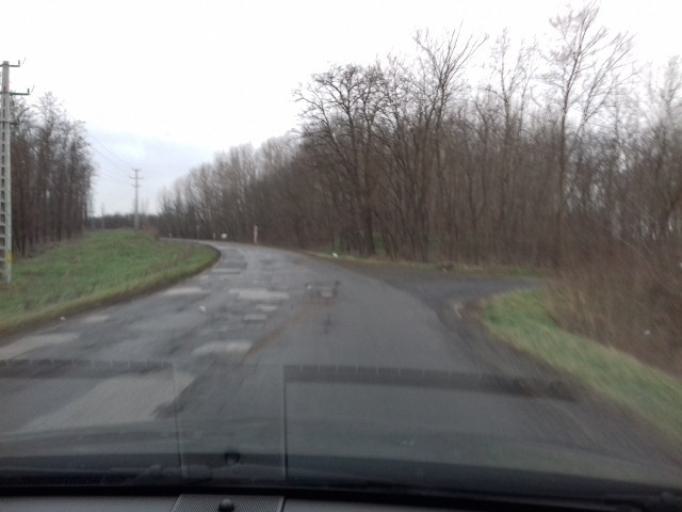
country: HU
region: Szabolcs-Szatmar-Bereg
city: Kek
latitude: 48.0877
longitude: 21.8656
